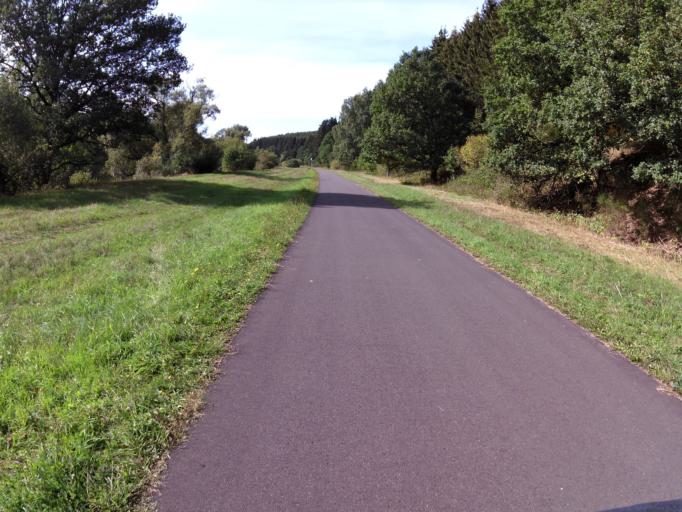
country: DE
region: Rheinland-Pfalz
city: Brandscheid
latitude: 50.1878
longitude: 6.3046
